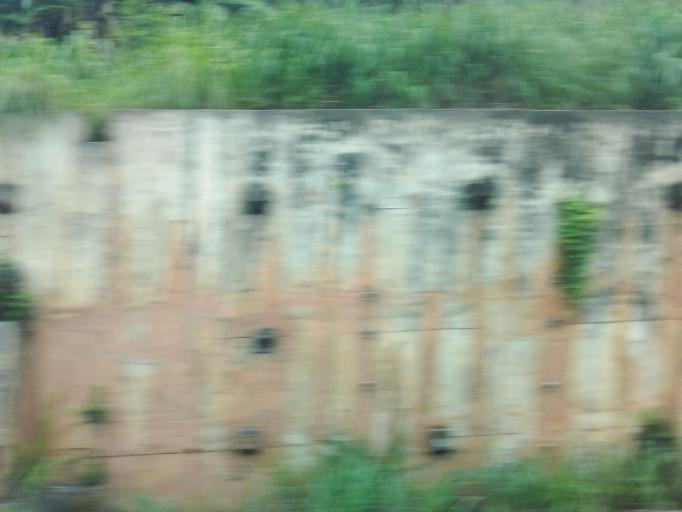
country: BR
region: Minas Gerais
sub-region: Joao Monlevade
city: Joao Monlevade
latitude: -19.8278
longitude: -43.1271
